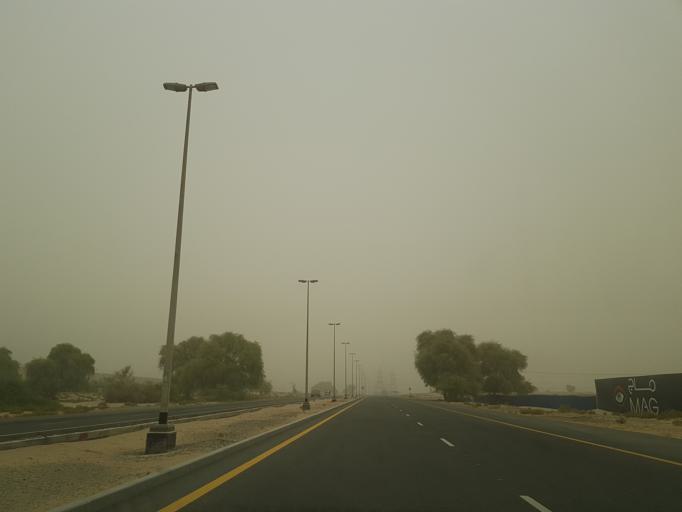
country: AE
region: Dubai
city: Dubai
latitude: 25.1448
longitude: 55.2877
